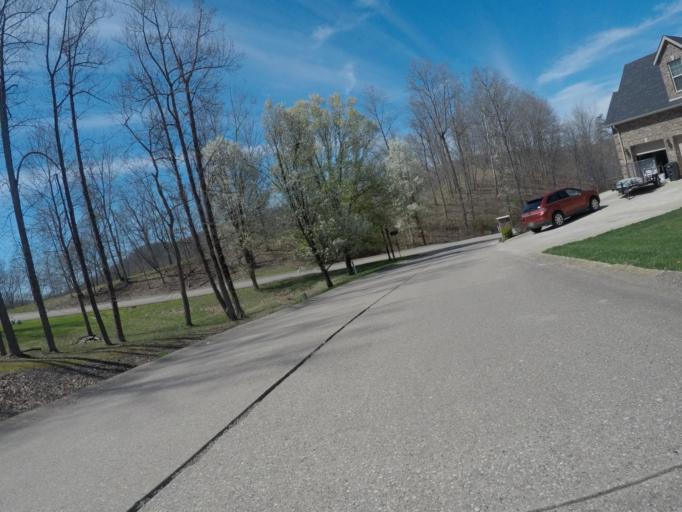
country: US
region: West Virginia
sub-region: Cabell County
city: Pea Ridge
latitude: 38.4041
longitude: -82.3117
